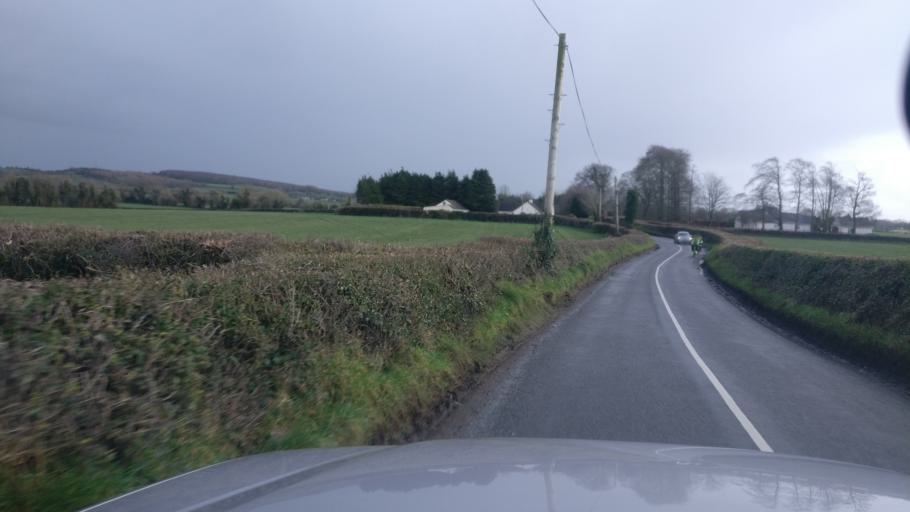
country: IE
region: Munster
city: Nenagh Bridge
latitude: 52.9582
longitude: -8.0770
